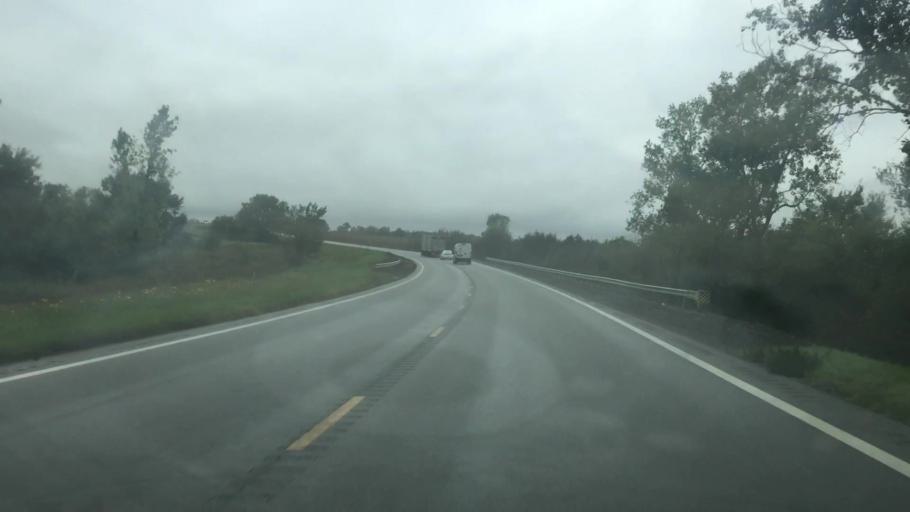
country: US
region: Kansas
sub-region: Anderson County
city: Garnett
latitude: 38.1616
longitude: -95.3077
